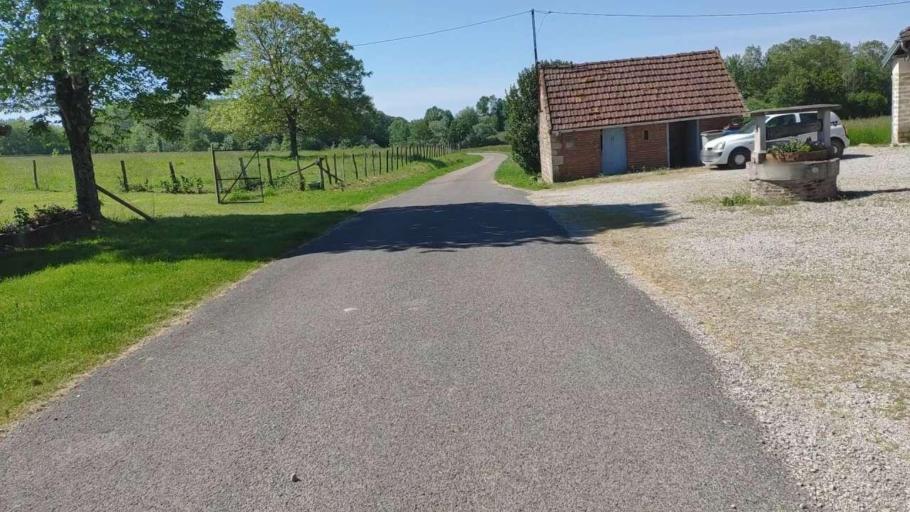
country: FR
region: Franche-Comte
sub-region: Departement du Jura
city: Bletterans
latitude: 46.7801
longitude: 5.4235
